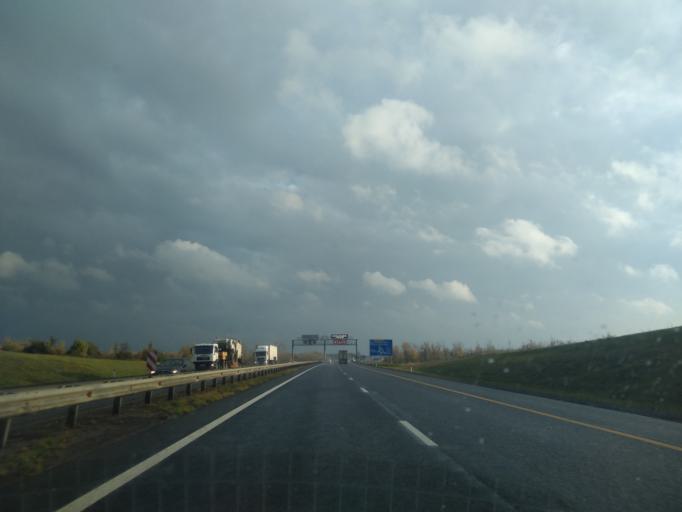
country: RU
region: Lipetsk
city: Yelets
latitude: 52.5593
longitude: 38.7134
